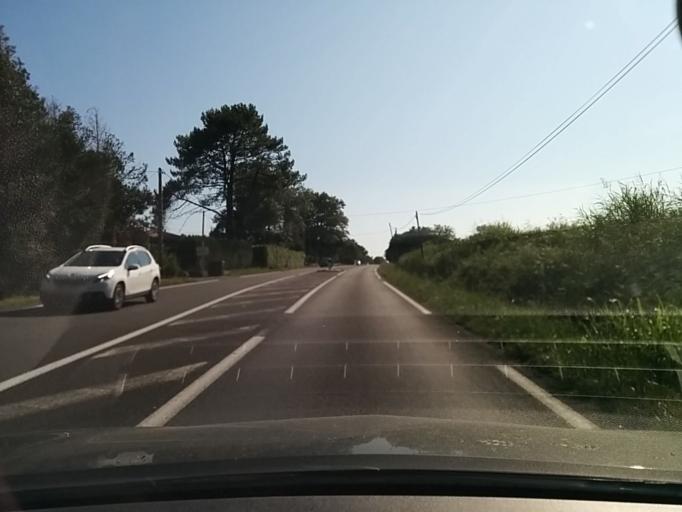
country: FR
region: Aquitaine
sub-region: Departement des Landes
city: Saint-Vincent-de-Tyrosse
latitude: 43.6498
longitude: -1.3259
